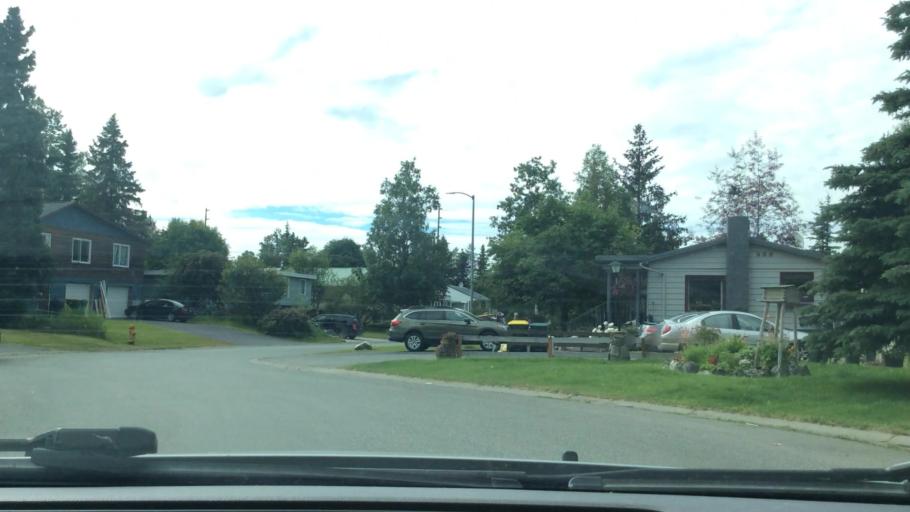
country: US
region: Alaska
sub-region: Anchorage Municipality
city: Anchorage
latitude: 61.2202
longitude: -149.7905
